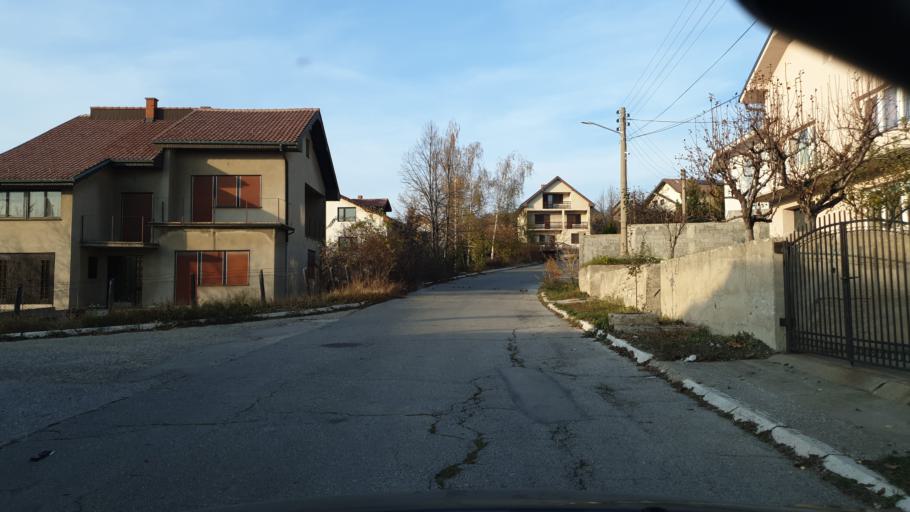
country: RS
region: Central Serbia
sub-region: Borski Okrug
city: Bor
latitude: 44.0571
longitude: 22.0816
